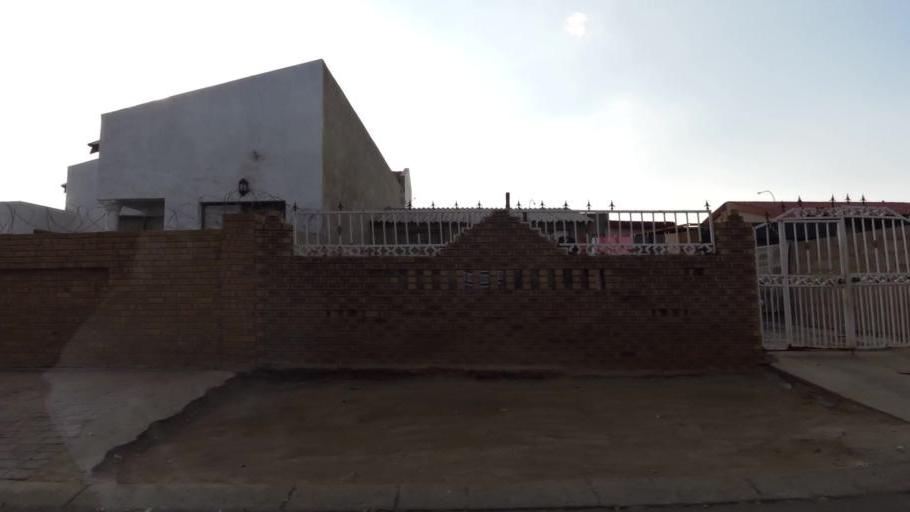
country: ZA
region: Gauteng
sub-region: City of Johannesburg Metropolitan Municipality
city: Roodepoort
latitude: -26.2199
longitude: 27.9034
